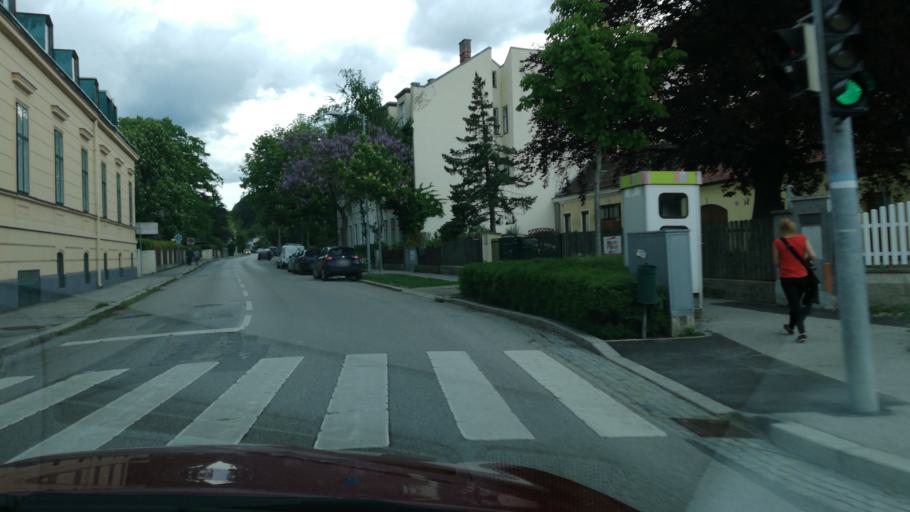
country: AT
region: Lower Austria
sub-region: Politischer Bezirk Baden
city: Baden
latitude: 48.0117
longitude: 16.2045
